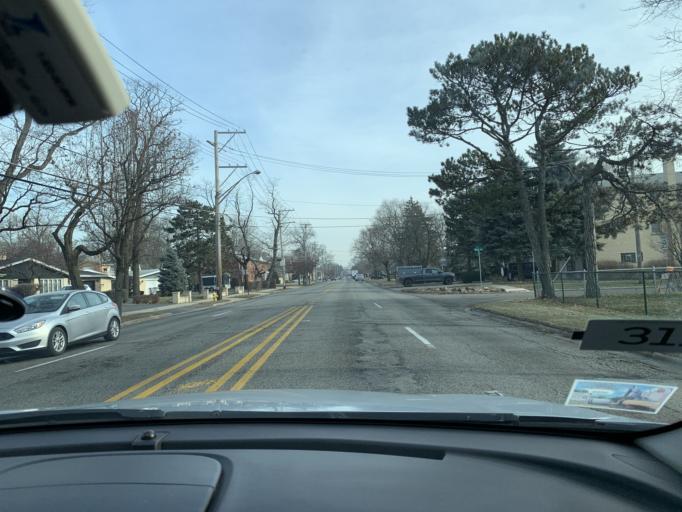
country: US
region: Illinois
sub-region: Cook County
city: Park Ridge
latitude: 42.0105
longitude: -87.8533
